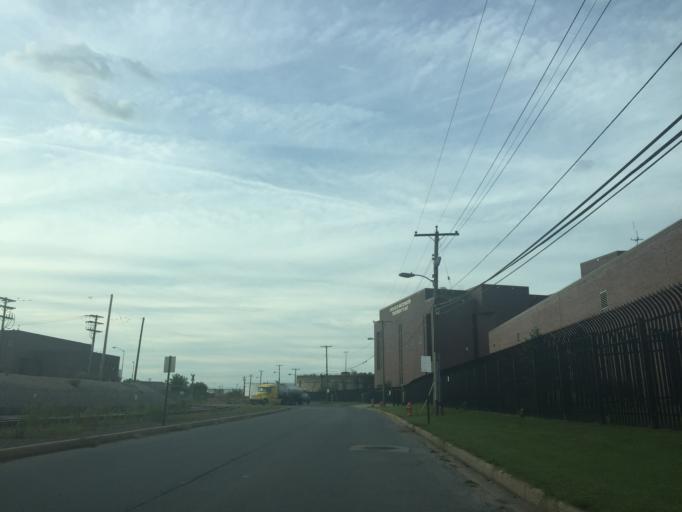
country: US
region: Maryland
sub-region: Anne Arundel County
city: Brooklyn Park
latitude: 39.2315
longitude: -76.5668
